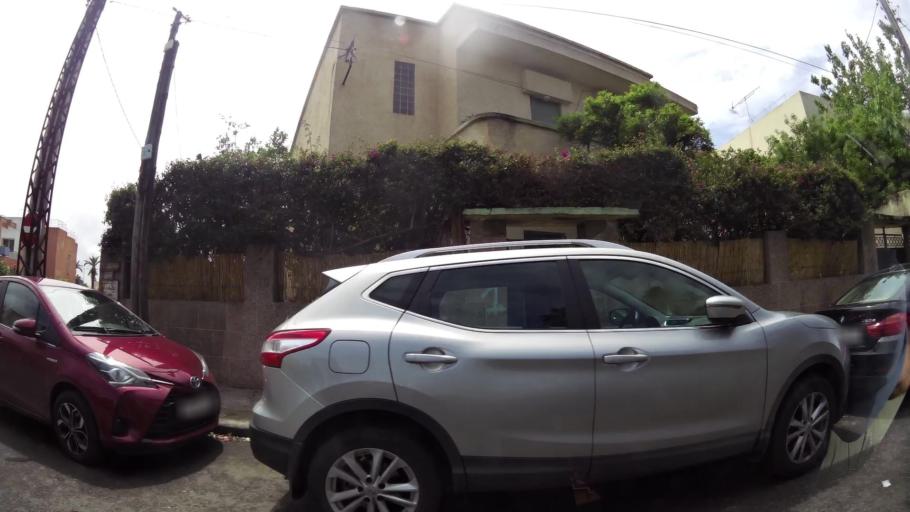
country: MA
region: Grand Casablanca
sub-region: Casablanca
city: Casablanca
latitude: 33.5650
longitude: -7.6349
